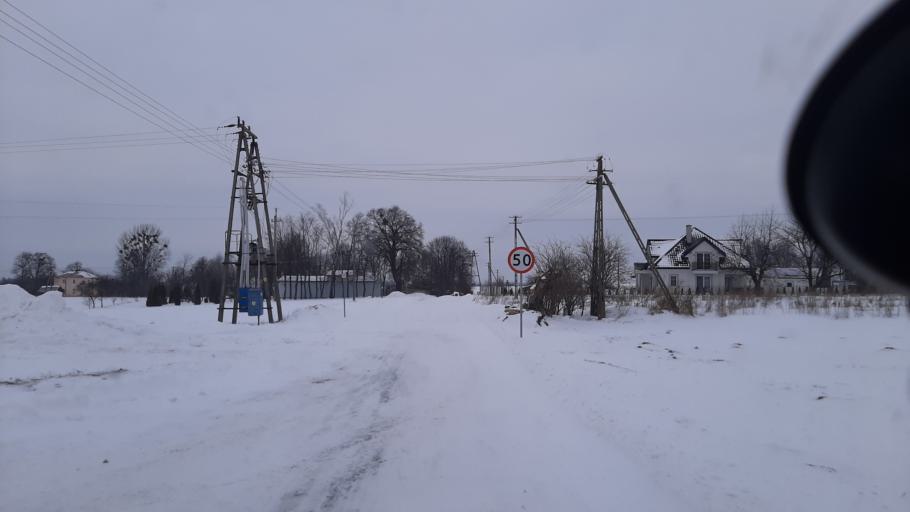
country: PL
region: Lublin Voivodeship
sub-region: Powiat lubelski
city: Garbow
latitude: 51.3320
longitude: 22.2911
